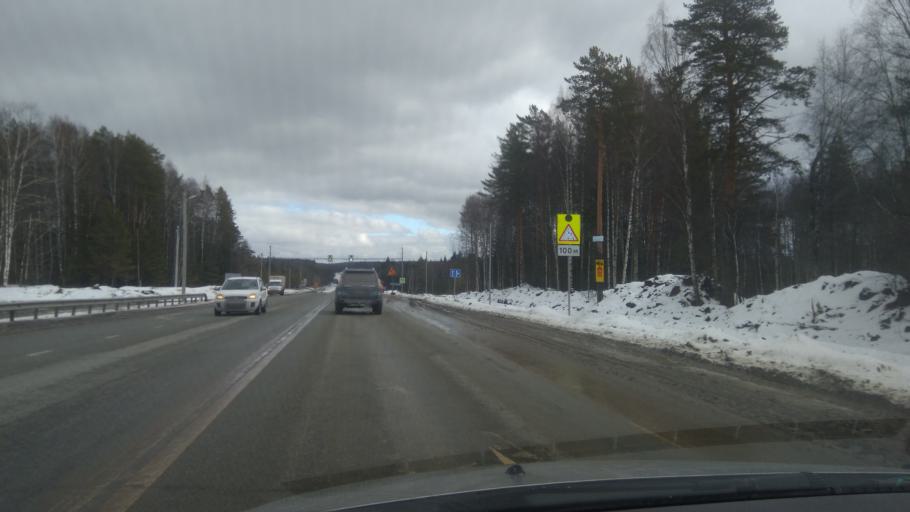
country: RU
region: Sverdlovsk
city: Bisert'
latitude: 56.8319
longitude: 58.9507
